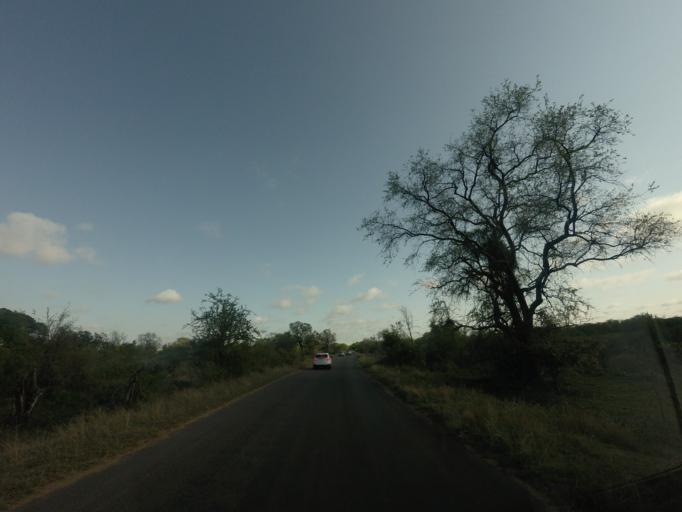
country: ZA
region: Mpumalanga
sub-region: Ehlanzeni District
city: Komatipoort
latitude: -25.2732
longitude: 31.8481
